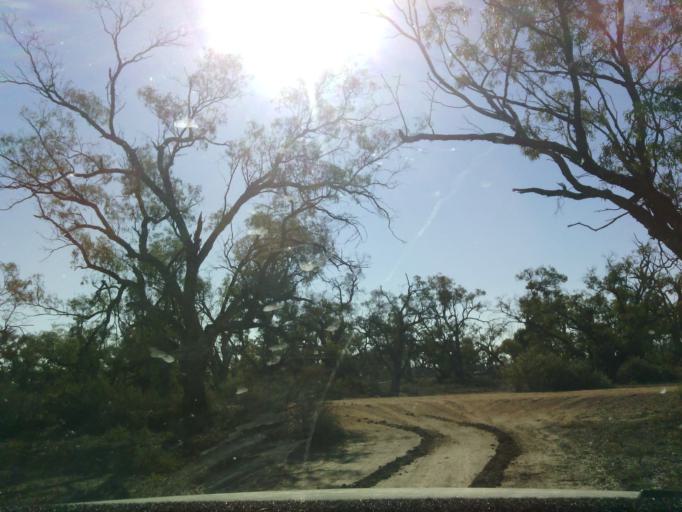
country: AU
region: South Australia
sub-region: Renmark Paringa
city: Renmark West
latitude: -34.2604
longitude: 140.6976
